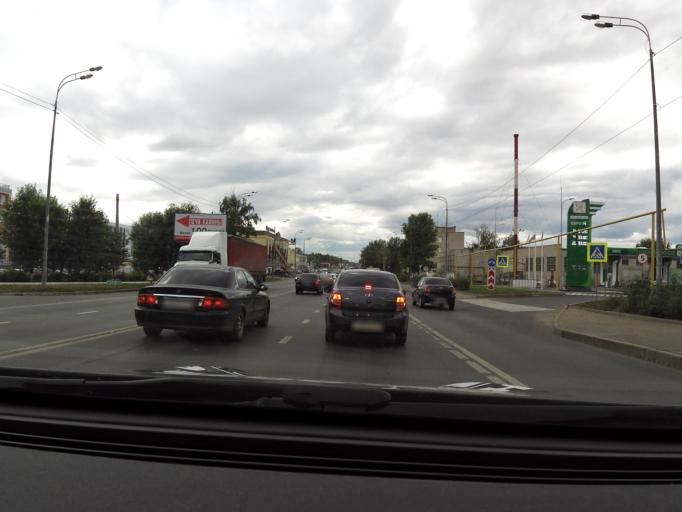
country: RU
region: Tatarstan
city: Staroye Arakchino
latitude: 55.8265
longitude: 49.0285
